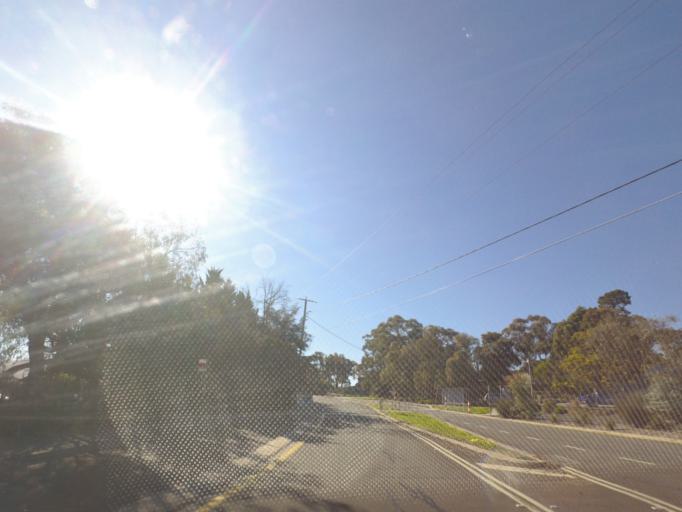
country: AU
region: Victoria
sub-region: Maroondah
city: Croydon Hills
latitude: -37.7669
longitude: 145.2718
